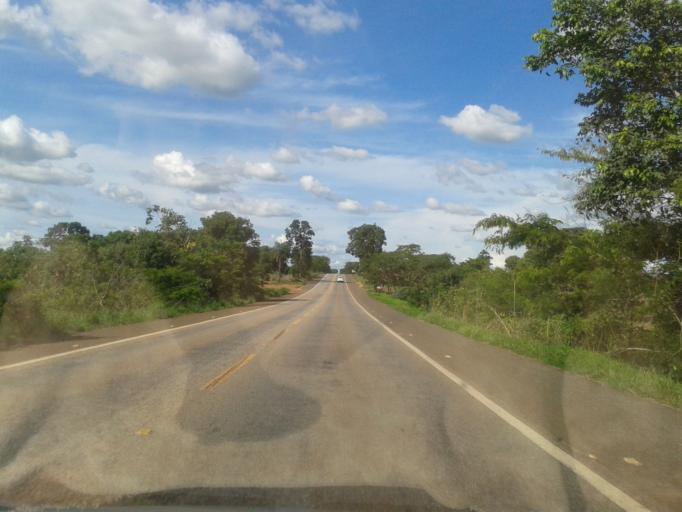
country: BR
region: Goias
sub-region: Mozarlandia
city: Mozarlandia
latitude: -15.0763
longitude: -50.6207
